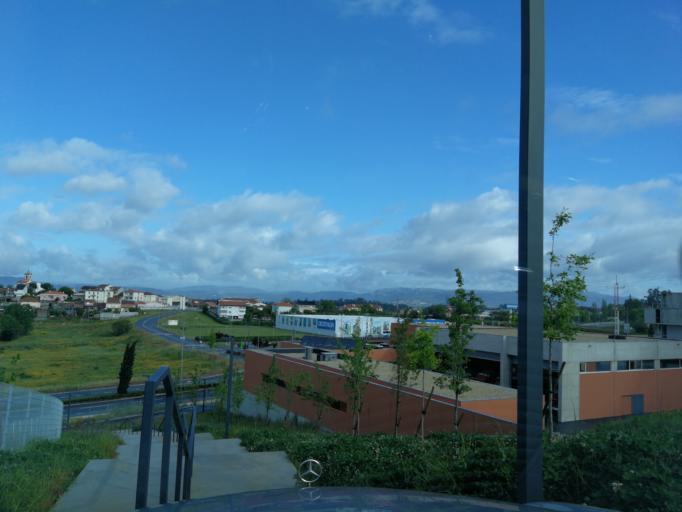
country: PT
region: Braga
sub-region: Braga
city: Braga
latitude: 41.5679
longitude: -8.4271
